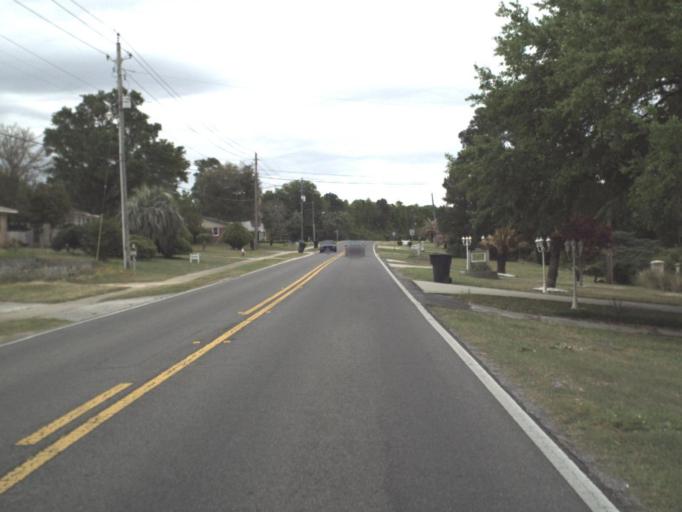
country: US
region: Florida
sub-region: Escambia County
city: East Pensacola Heights
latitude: 30.4478
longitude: -87.1860
